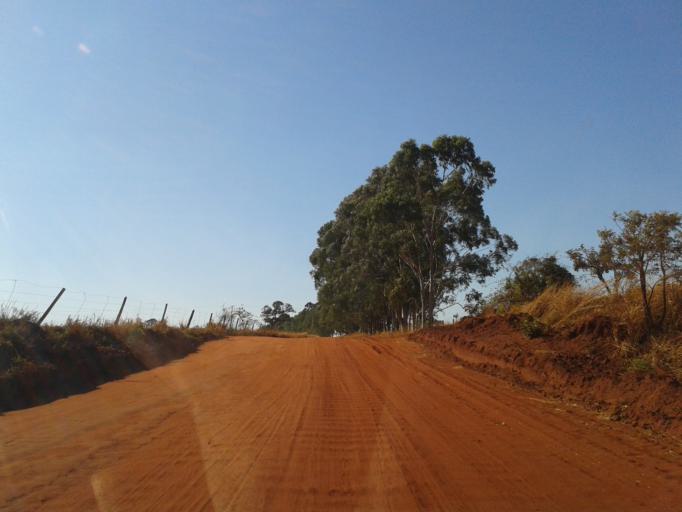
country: BR
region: Minas Gerais
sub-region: Ituiutaba
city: Ituiutaba
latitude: -18.9917
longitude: -49.3831
